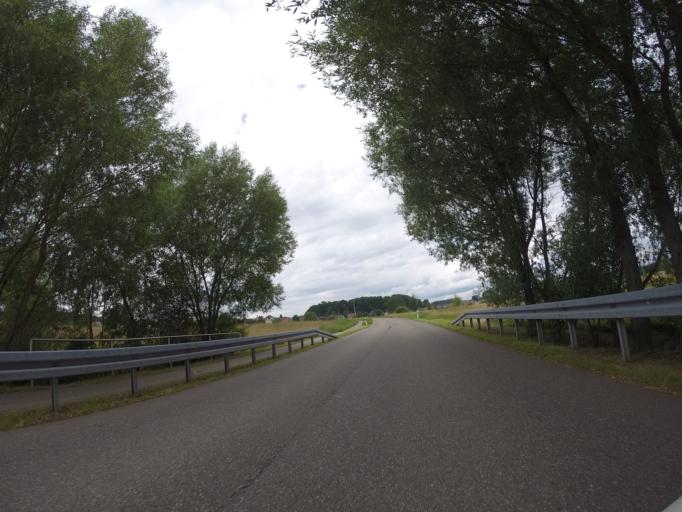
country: DE
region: Baden-Wuerttemberg
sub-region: Karlsruhe Region
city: Dobel
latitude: 48.8544
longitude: 8.5233
